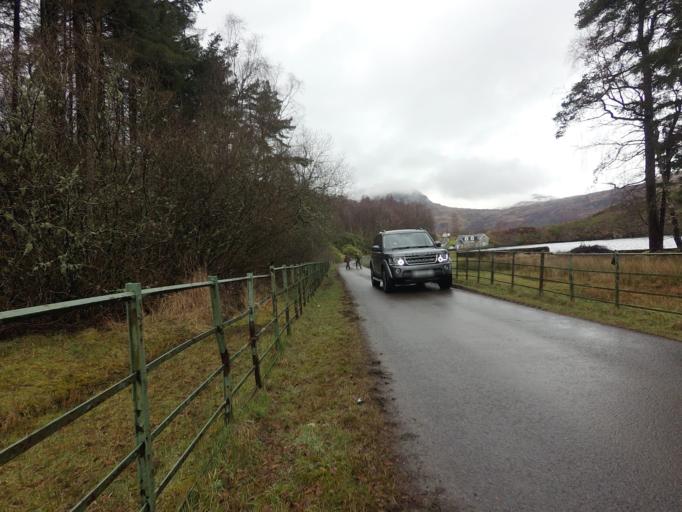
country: GB
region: Scotland
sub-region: West Dunbartonshire
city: Balloch
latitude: 56.2593
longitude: -4.5808
